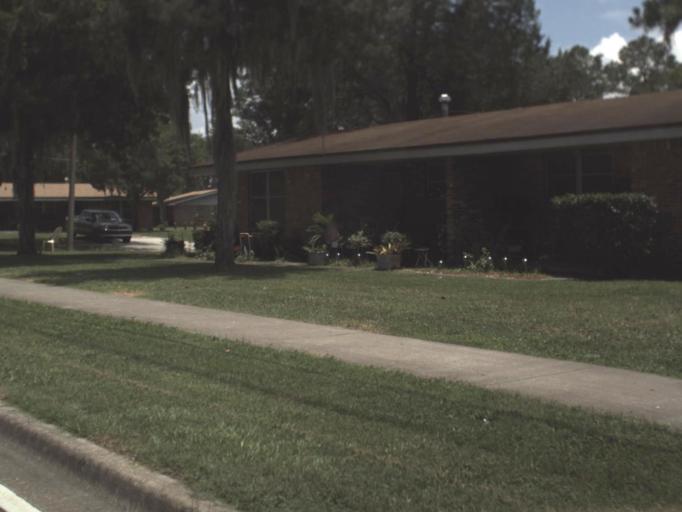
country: US
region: Florida
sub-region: Alachua County
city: Gainesville
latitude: 29.6518
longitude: -82.2910
